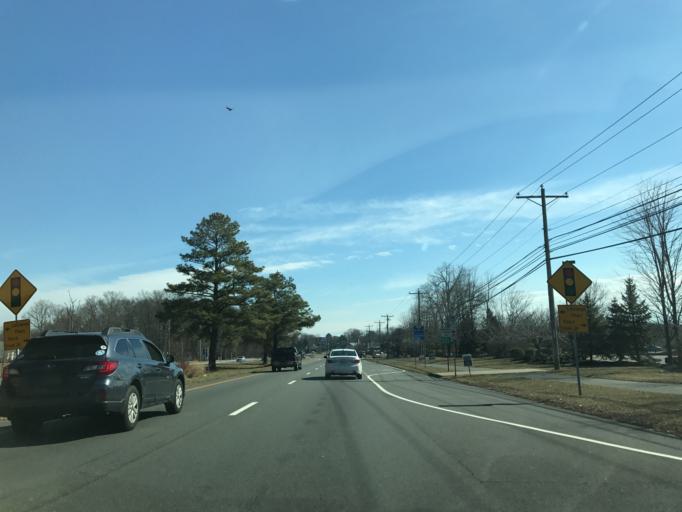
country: US
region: Delaware
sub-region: New Castle County
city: Glasgow
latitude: 39.6039
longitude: -75.7648
